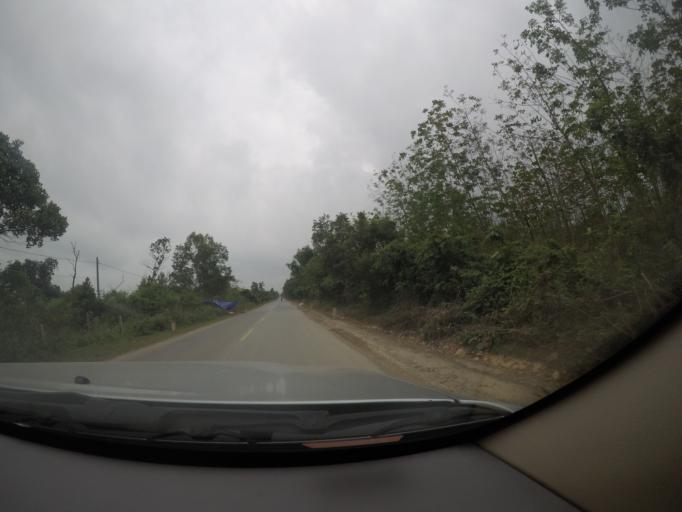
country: VN
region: Quang Binh
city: Kien Giang
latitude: 17.1908
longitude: 106.7268
